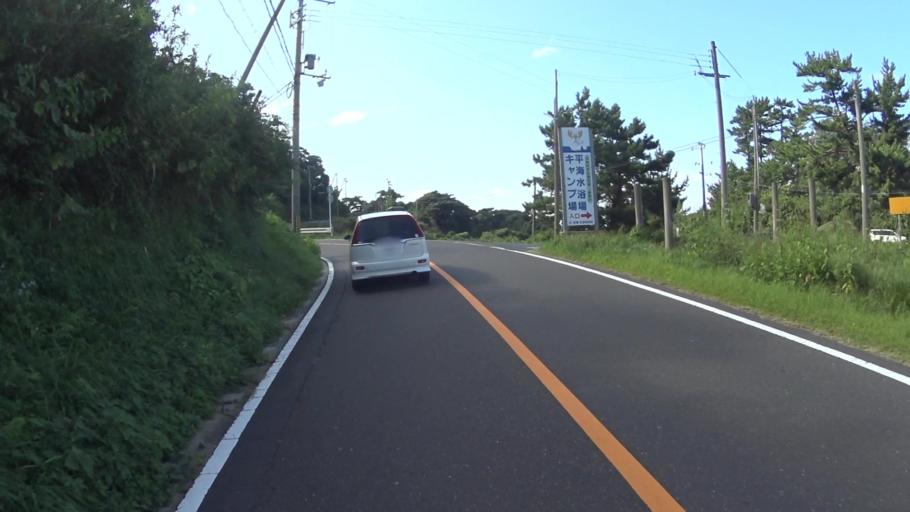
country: JP
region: Kyoto
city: Miyazu
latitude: 35.7514
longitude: 135.1583
